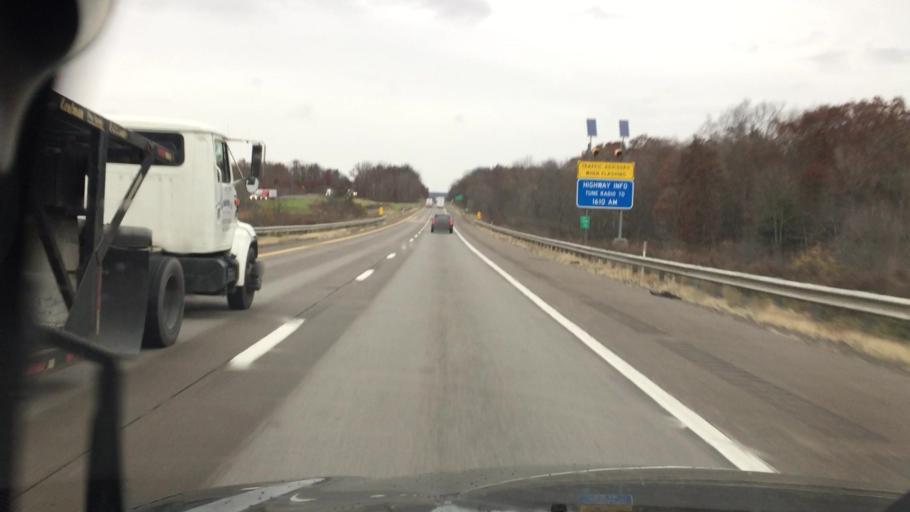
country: US
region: Pennsylvania
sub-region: Luzerne County
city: Mountain Top
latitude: 41.1112
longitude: -75.9607
